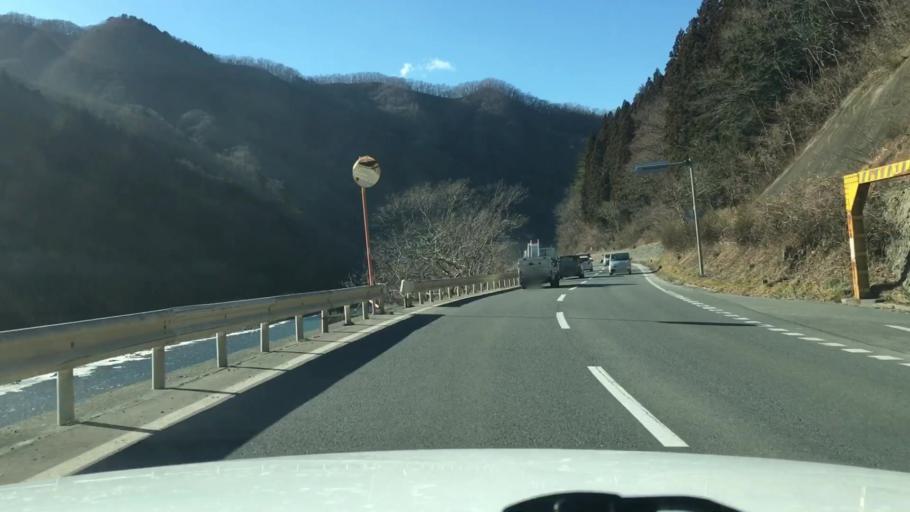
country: JP
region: Iwate
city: Miyako
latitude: 39.6228
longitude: 141.8318
